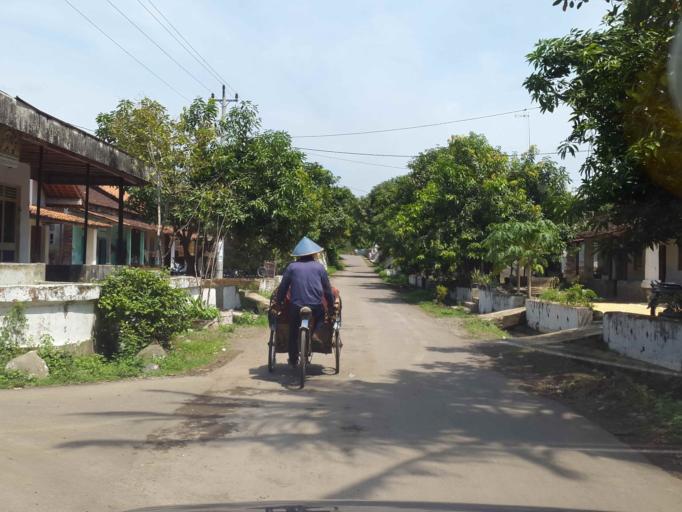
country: ID
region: Central Java
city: Margasari
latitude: -7.1084
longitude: 109.0144
